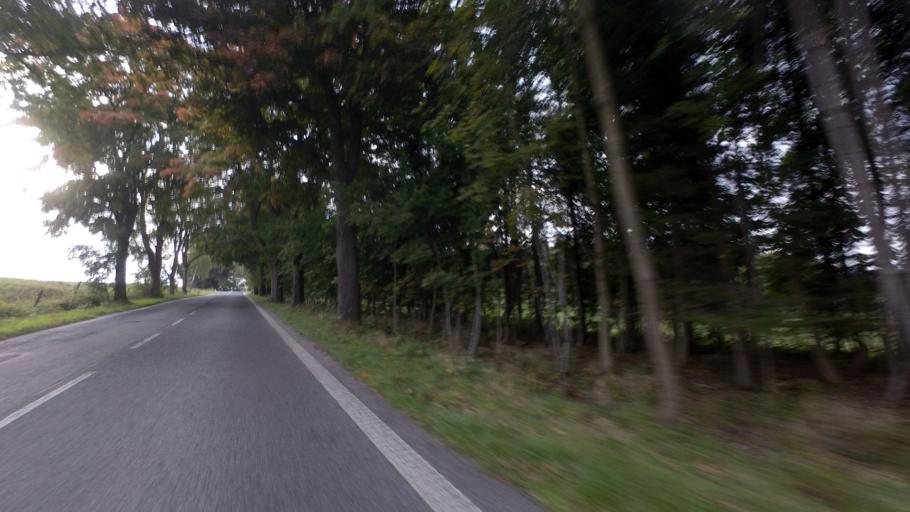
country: CZ
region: Ustecky
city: Vilemov
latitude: 51.0158
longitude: 14.3304
